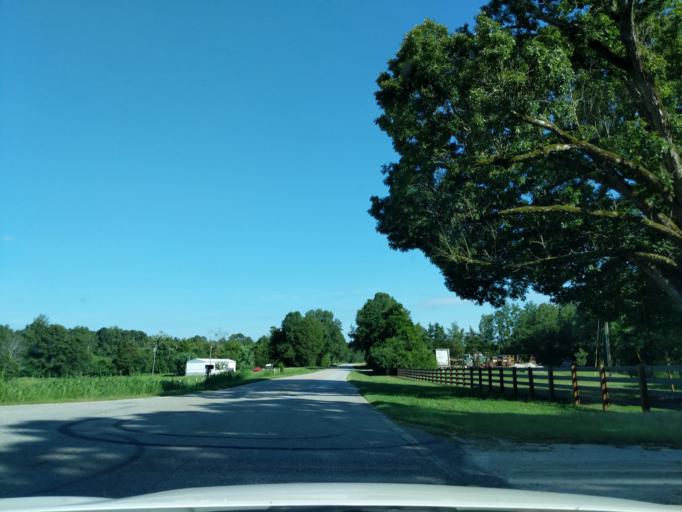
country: US
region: Georgia
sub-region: Oglethorpe County
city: Lexington
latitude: 33.9250
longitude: -83.0328
